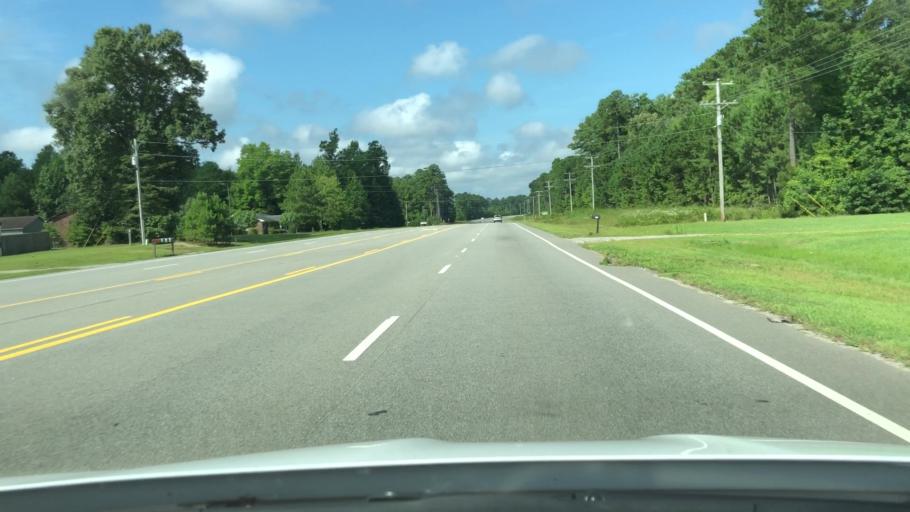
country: US
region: North Carolina
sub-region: Bertie County
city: Windsor
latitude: 36.0205
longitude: -76.8251
